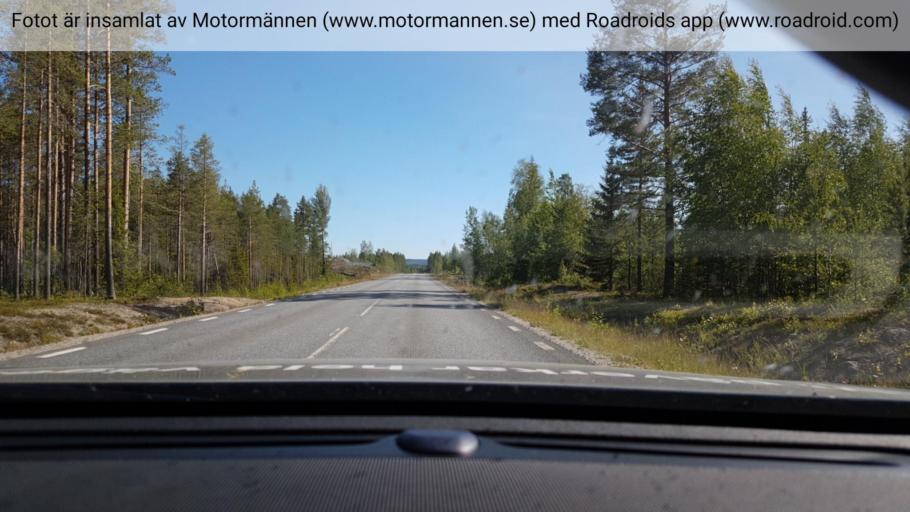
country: SE
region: Vaesterbotten
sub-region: Lycksele Kommun
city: Lycksele
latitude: 64.4993
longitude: 18.8979
